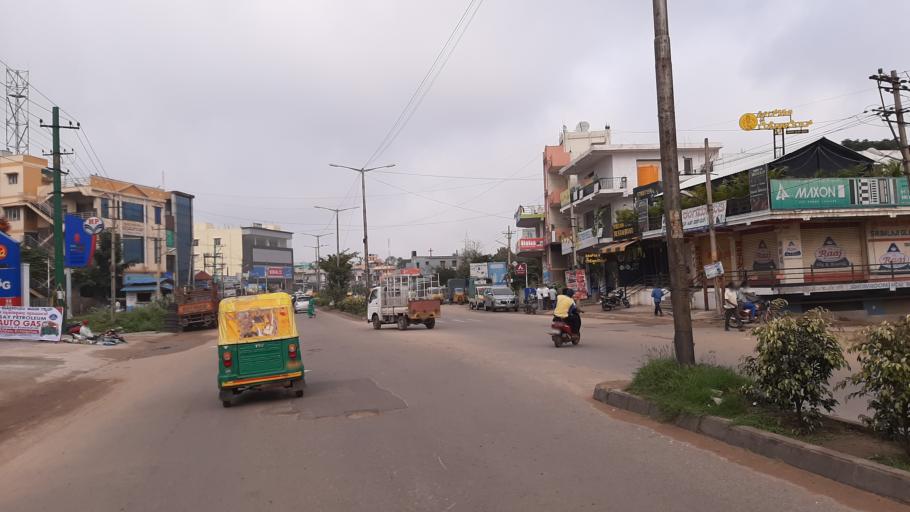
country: IN
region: Karnataka
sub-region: Bangalore Urban
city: Bangalore
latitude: 12.9853
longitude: 77.4853
